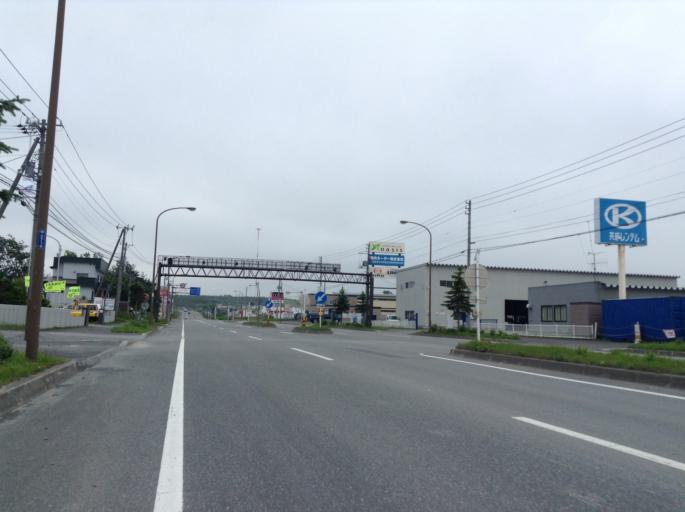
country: JP
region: Hokkaido
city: Wakkanai
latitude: 45.3819
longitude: 141.7088
